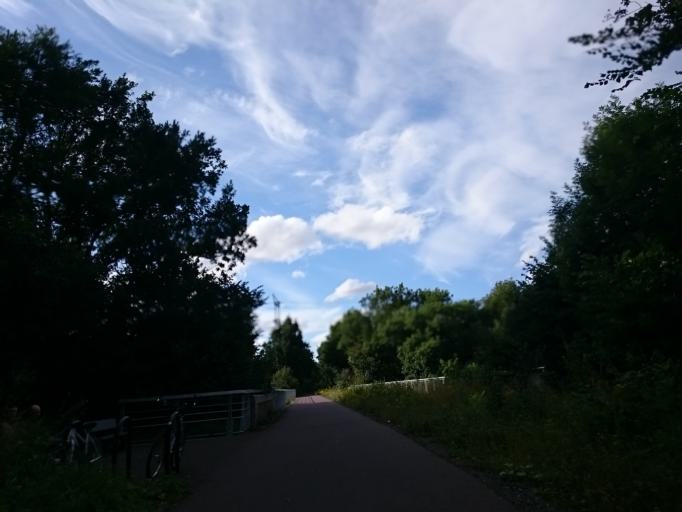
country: FR
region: Lower Normandy
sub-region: Departement du Calvados
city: Saint-Andre-sur-Orne
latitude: 49.1248
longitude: -0.4008
